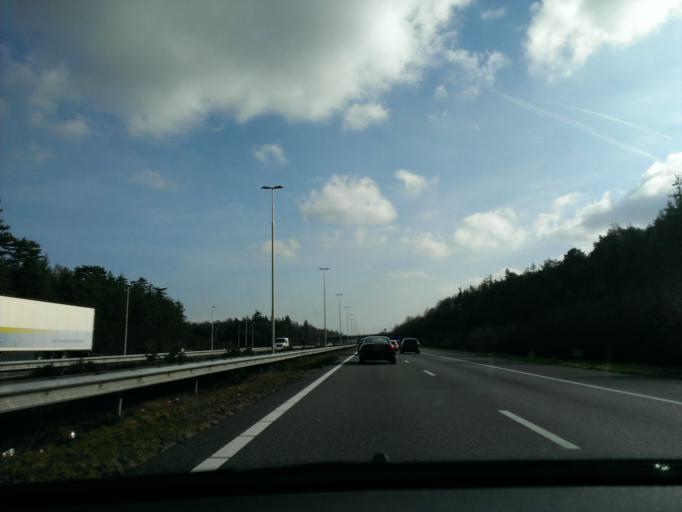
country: NL
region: Gelderland
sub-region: Gemeente Heerde
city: Heerde
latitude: 52.4174
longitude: 6.0162
